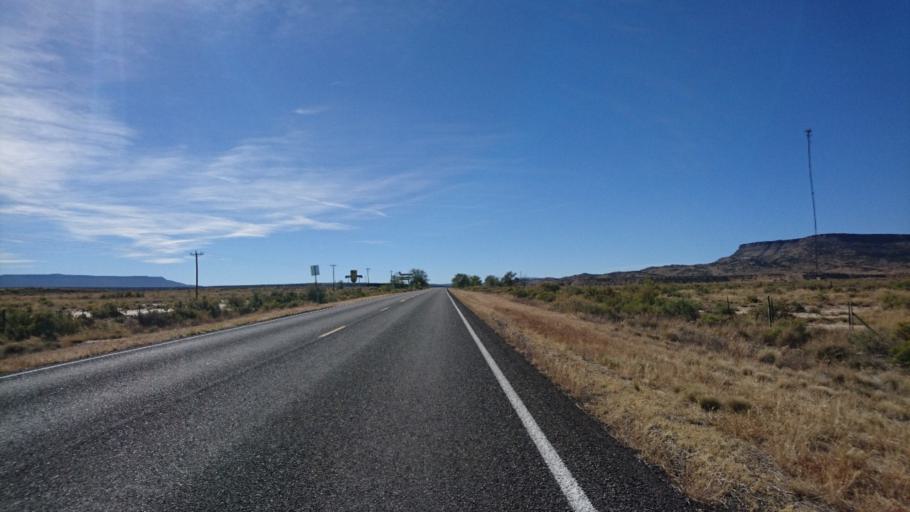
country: US
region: New Mexico
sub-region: Cibola County
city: Skyline-Ganipa
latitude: 35.0785
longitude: -107.6424
